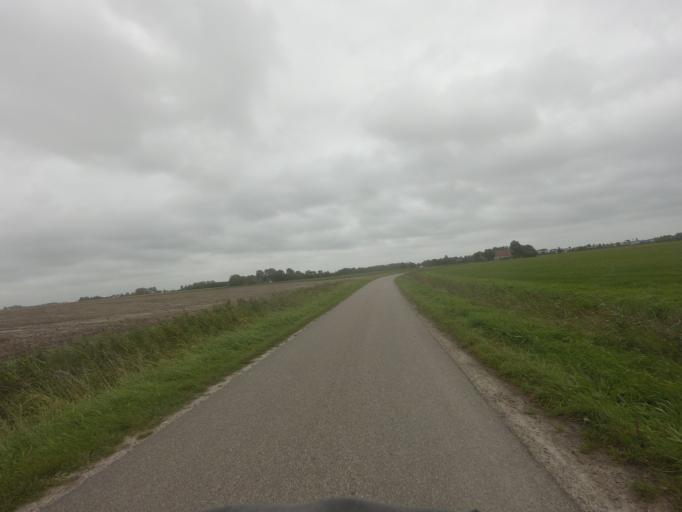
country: NL
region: Friesland
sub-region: Gemeente Leeuwarderadeel
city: Stiens
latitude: 53.2735
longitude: 5.7510
